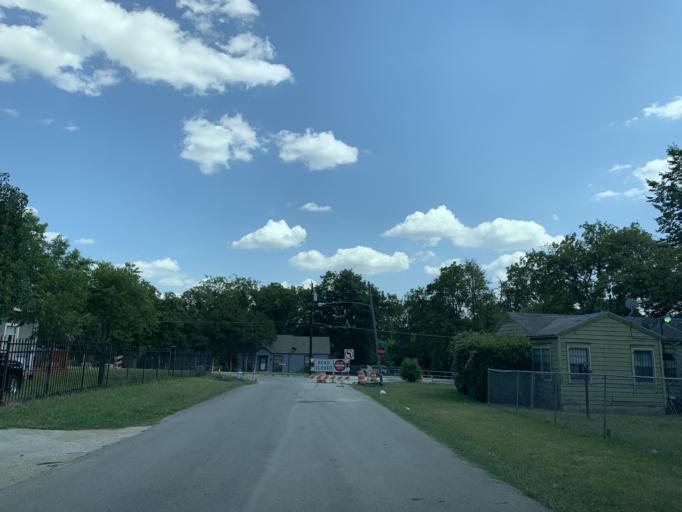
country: US
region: Texas
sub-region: Dallas County
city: Dallas
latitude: 32.7131
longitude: -96.7702
